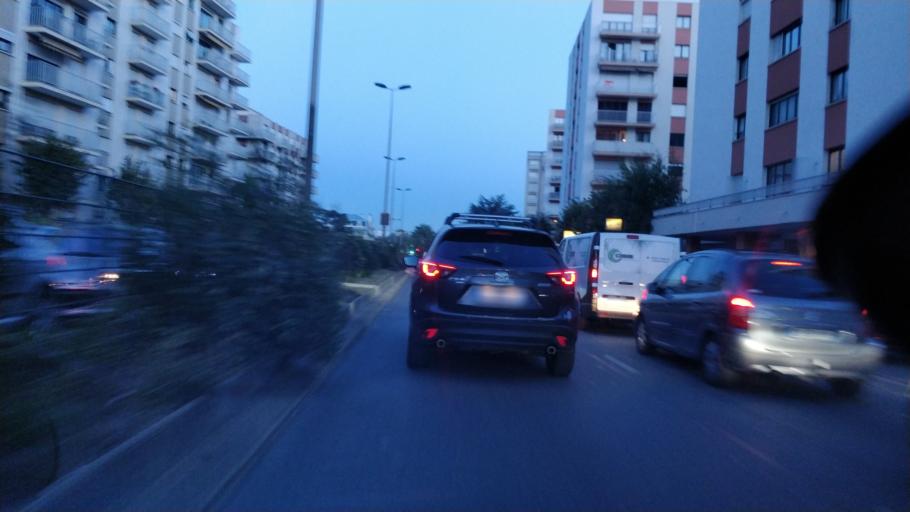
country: FR
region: Ile-de-France
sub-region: Departement de Seine-Saint-Denis
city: Villemomble
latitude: 48.8844
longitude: 2.5082
